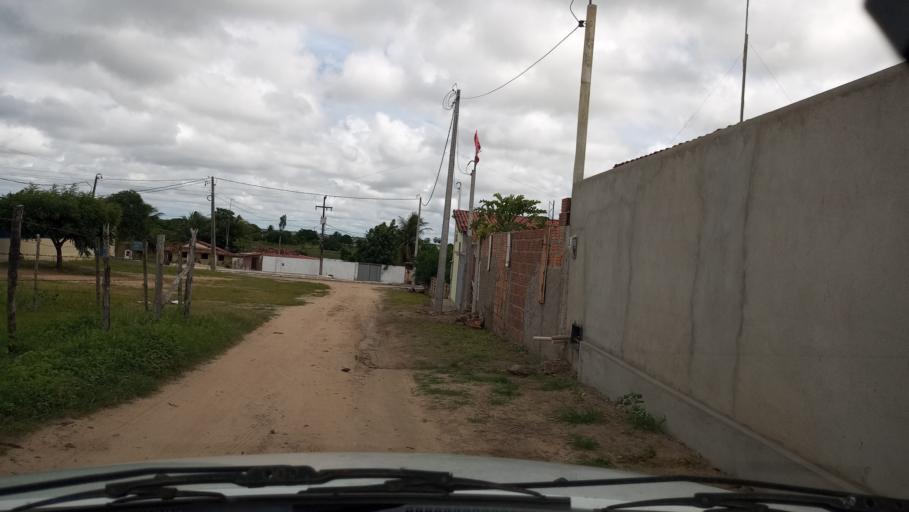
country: BR
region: Rio Grande do Norte
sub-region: Brejinho
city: Brejinho
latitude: -6.1538
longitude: -35.4379
